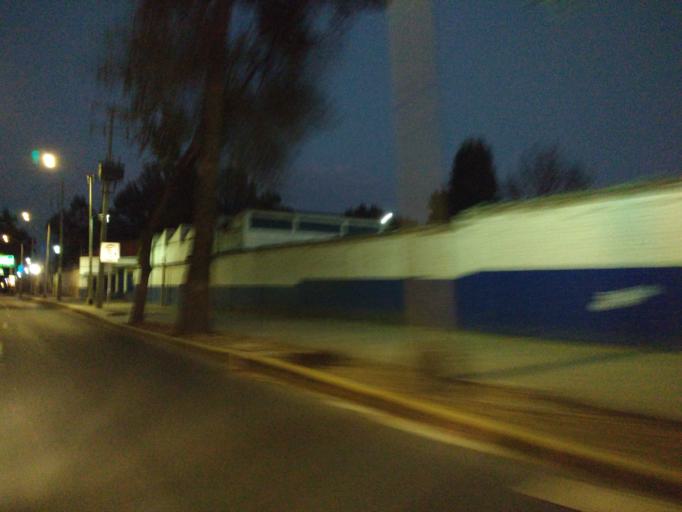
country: MX
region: Mexico City
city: Tlalpan
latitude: 19.2868
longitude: -99.1562
